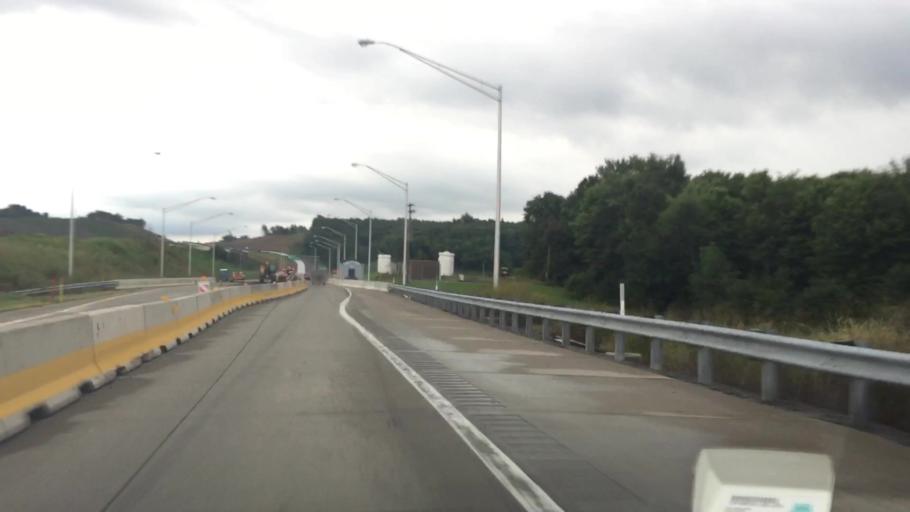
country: US
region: Pennsylvania
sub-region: Allegheny County
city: Imperial
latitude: 40.4282
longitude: -80.3201
